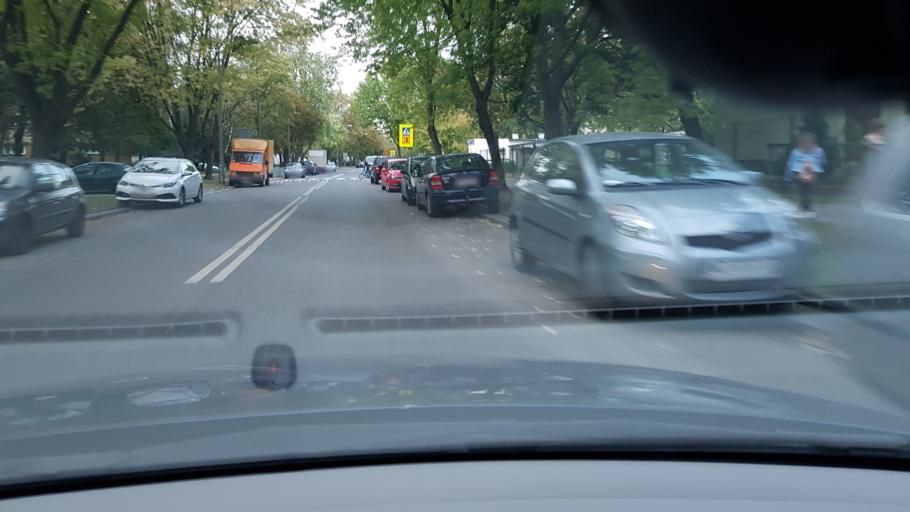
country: PL
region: Masovian Voivodeship
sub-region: Warszawa
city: Bielany
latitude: 52.2930
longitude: 20.9359
